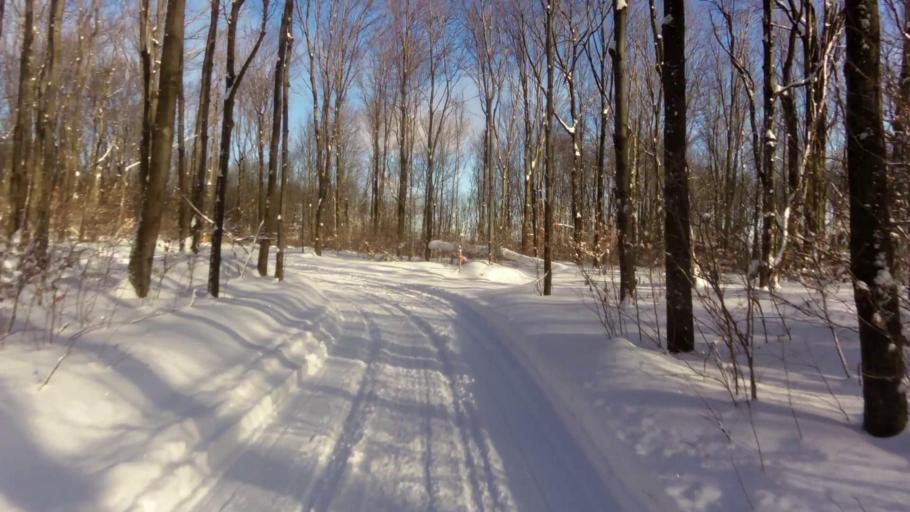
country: US
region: New York
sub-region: Chautauqua County
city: Falconer
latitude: 42.2767
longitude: -79.1284
